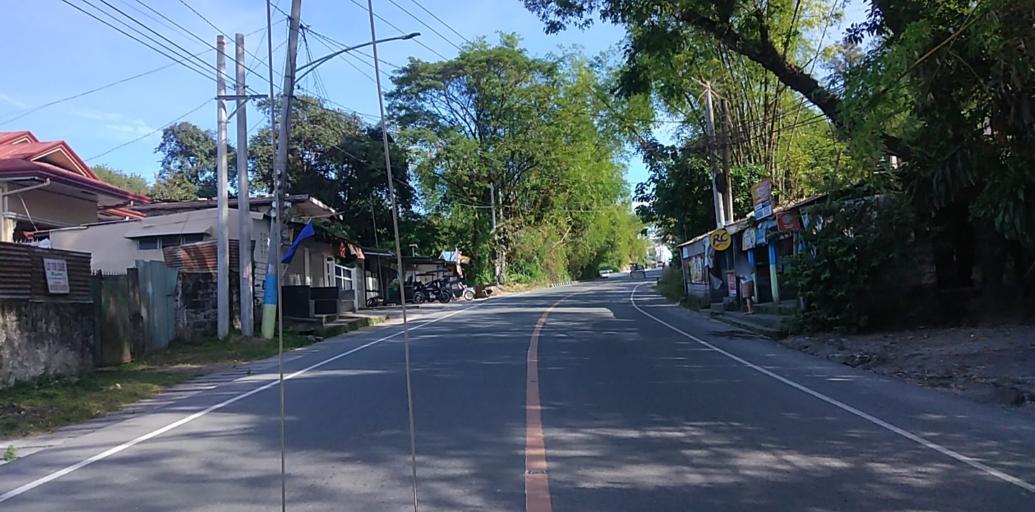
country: PH
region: Central Luzon
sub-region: Province of Pampanga
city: Porac
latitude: 15.0769
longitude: 120.5442
